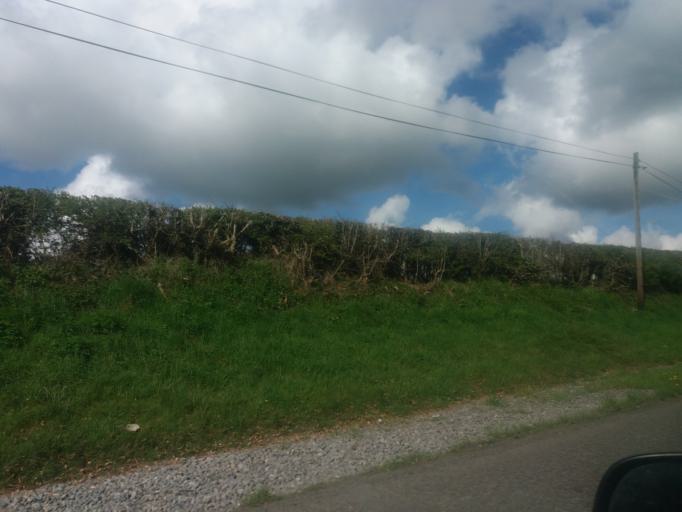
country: IE
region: Ulster
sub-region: An Cabhan
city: Virginia
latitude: 53.8730
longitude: -7.1227
